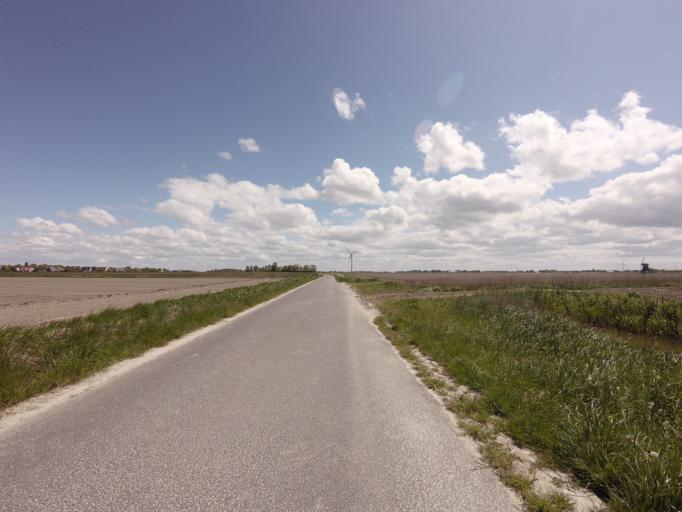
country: NL
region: Friesland
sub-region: Gemeente Harlingen
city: Harlingen
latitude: 53.1382
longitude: 5.4255
